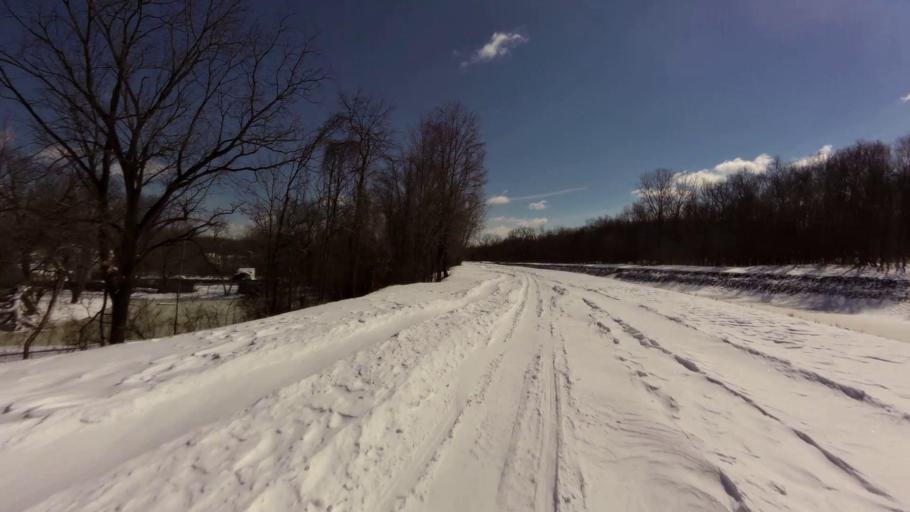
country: US
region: New York
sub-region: Orleans County
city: Holley
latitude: 43.2532
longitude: -78.0754
